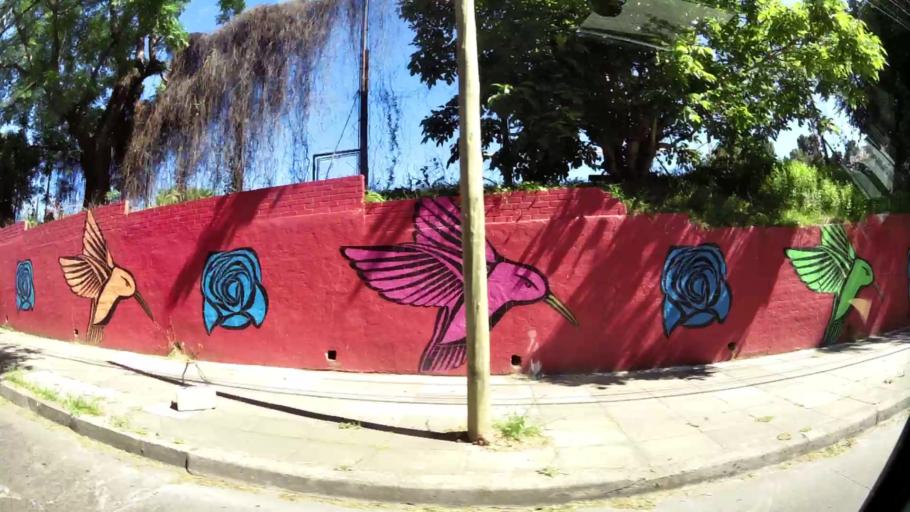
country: AR
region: Buenos Aires
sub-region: Partido de Vicente Lopez
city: Olivos
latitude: -34.5213
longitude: -58.4783
